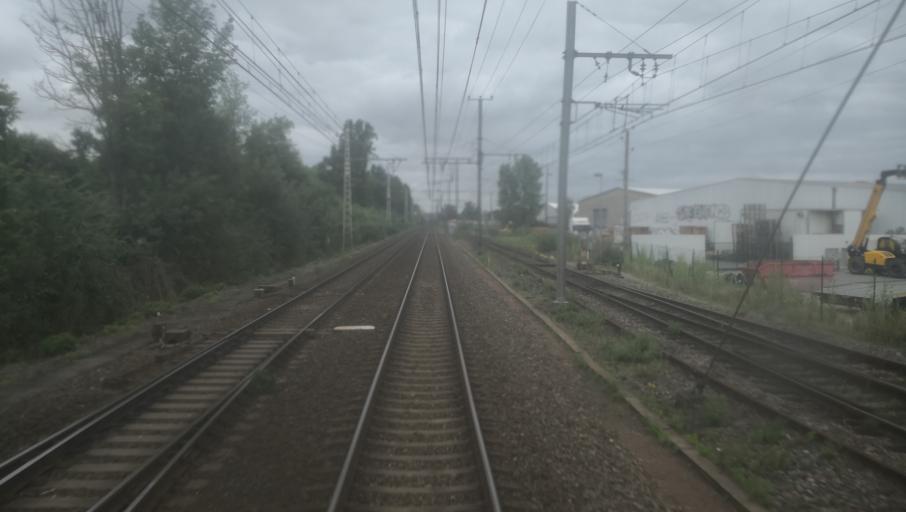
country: FR
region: Midi-Pyrenees
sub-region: Departement de la Haute-Garonne
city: Lespinasse
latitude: 43.7200
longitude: 1.3819
